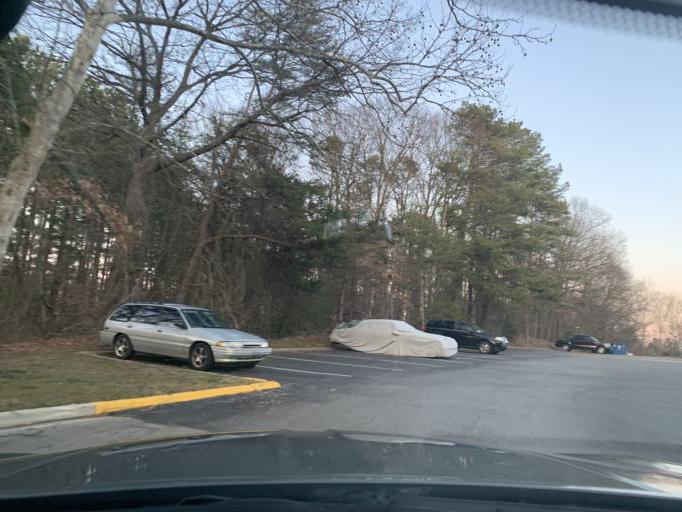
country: US
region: Maryland
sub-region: Anne Arundel County
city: Glen Burnie
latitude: 39.1519
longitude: -76.6419
